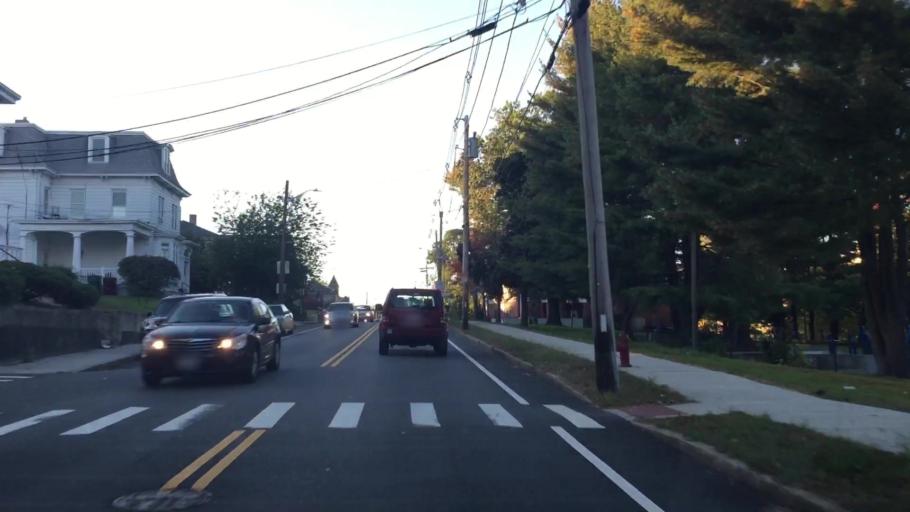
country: US
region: Massachusetts
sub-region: Middlesex County
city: Lowell
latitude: 42.6462
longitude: -71.3224
